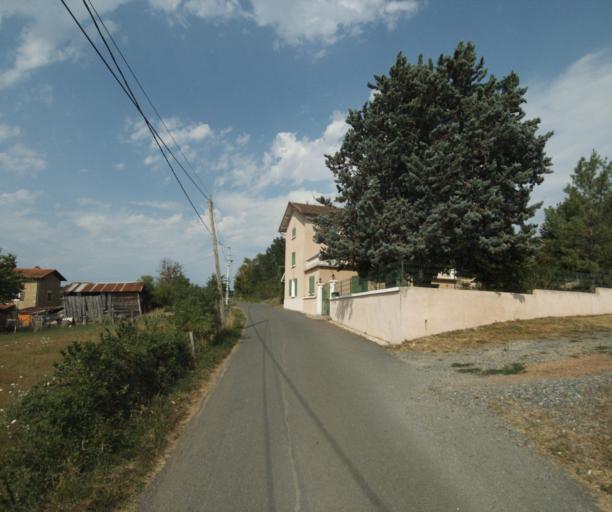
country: FR
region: Rhone-Alpes
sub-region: Departement du Rhone
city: Bully
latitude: 45.8464
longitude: 4.5933
